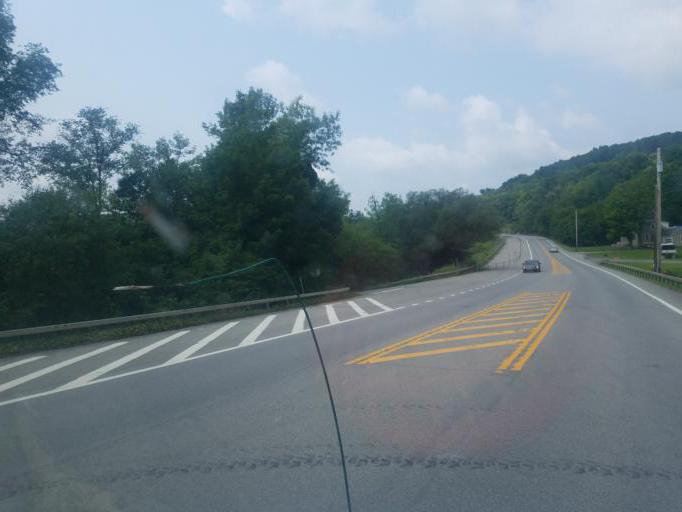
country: US
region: New York
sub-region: Herkimer County
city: Little Falls
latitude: 43.0374
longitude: -74.8194
